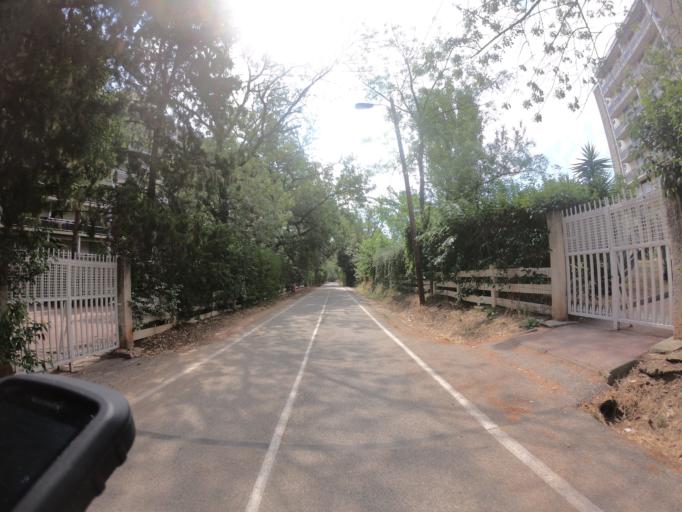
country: FR
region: Provence-Alpes-Cote d'Azur
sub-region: Departement du Var
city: La Valette-du-Var
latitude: 43.1173
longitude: 5.9723
